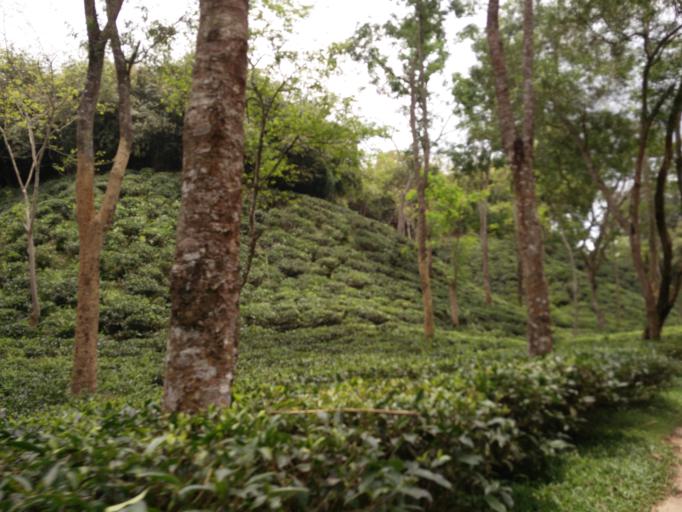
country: IN
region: Tripura
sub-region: Dhalai
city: Kamalpur
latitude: 24.3055
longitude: 91.8024
